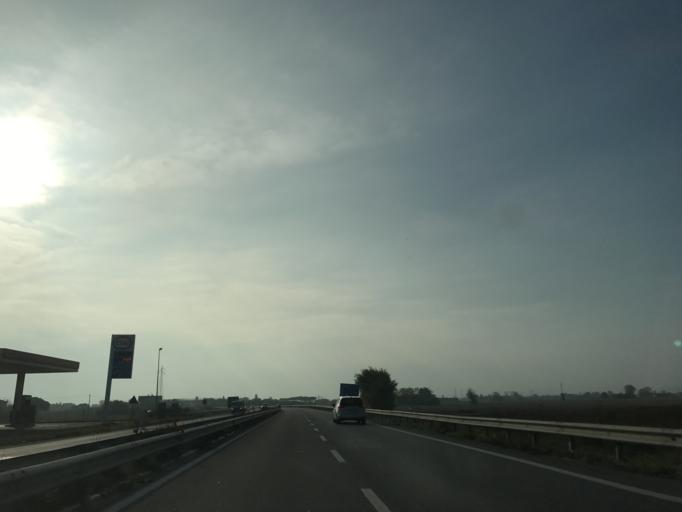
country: IT
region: Emilia-Romagna
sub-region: Provincia di Rimini
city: Bellaria-Igea Marina
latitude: 44.1189
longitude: 12.4739
